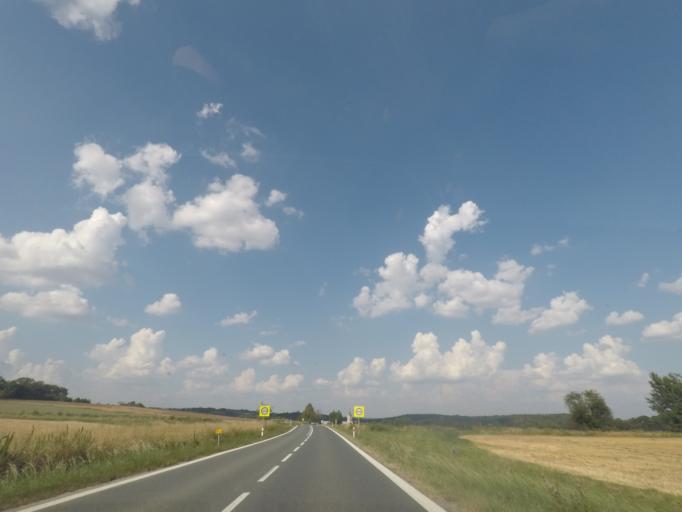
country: CZ
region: Kralovehradecky
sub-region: Okres Nachod
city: Jaromer
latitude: 50.3735
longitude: 15.9128
